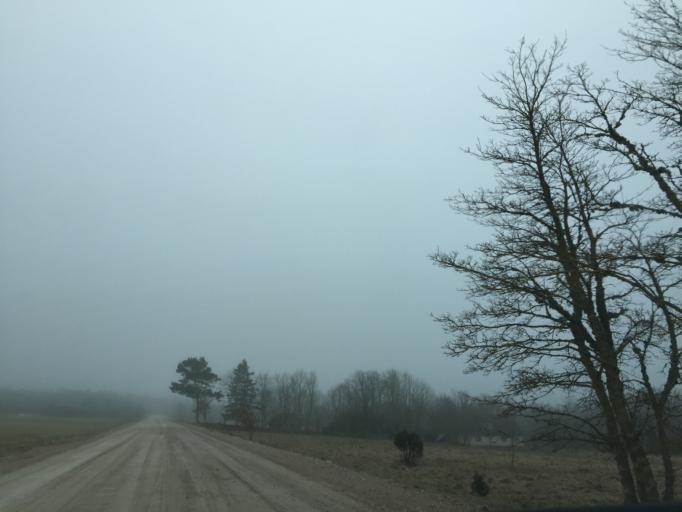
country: EE
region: Saare
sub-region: Kuressaare linn
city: Kuressaare
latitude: 58.4931
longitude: 21.9847
